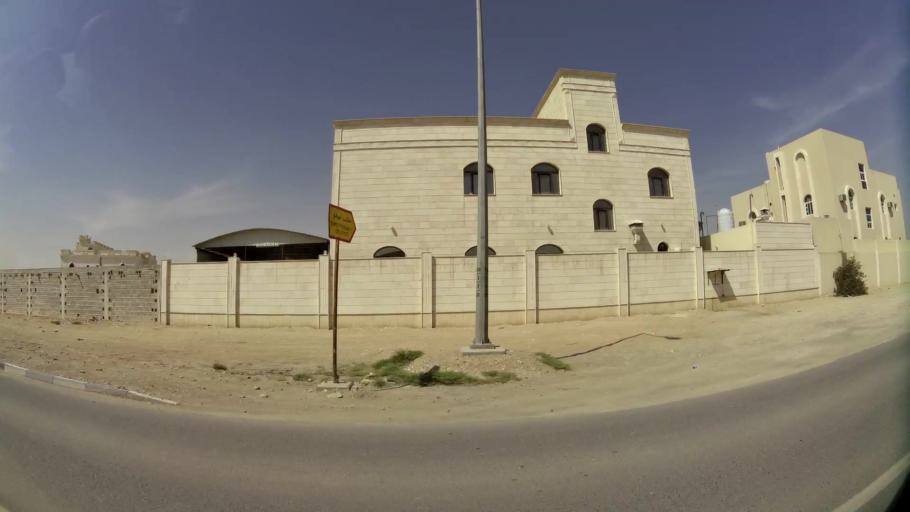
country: QA
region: Baladiyat ar Rayyan
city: Ar Rayyan
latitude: 25.2482
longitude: 51.3887
